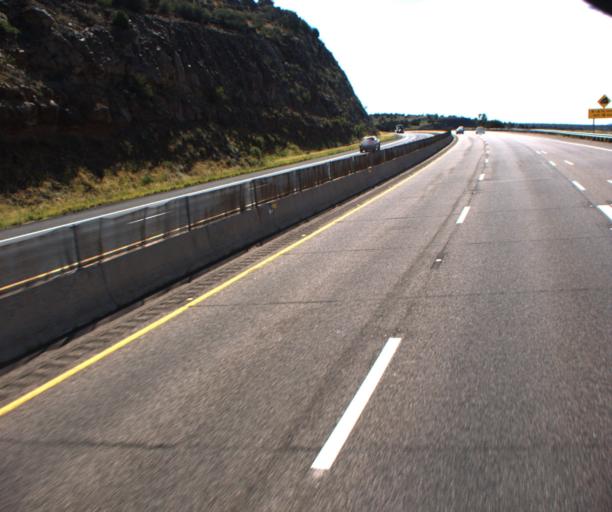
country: US
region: Arizona
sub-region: Yavapai County
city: Village of Oak Creek (Big Park)
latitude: 34.8102
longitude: -111.6063
